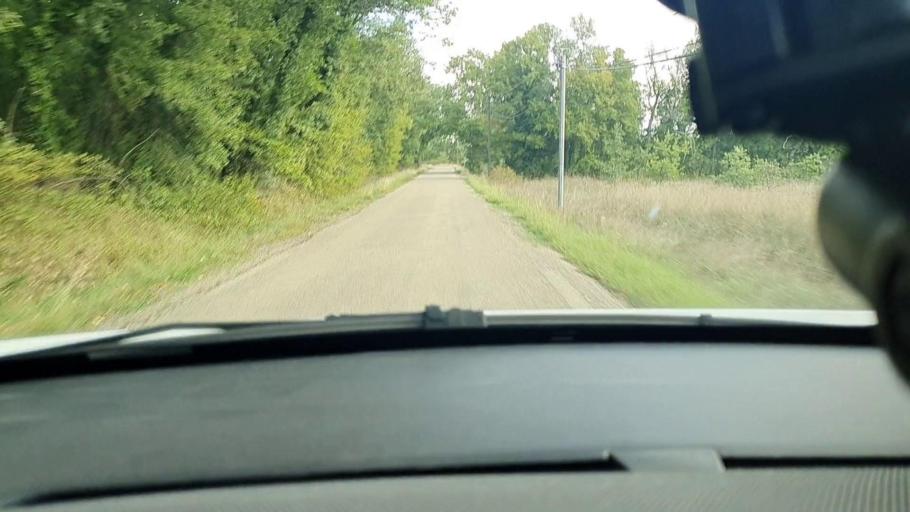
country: FR
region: Languedoc-Roussillon
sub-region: Departement du Gard
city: Mons
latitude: 44.1653
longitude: 4.2945
